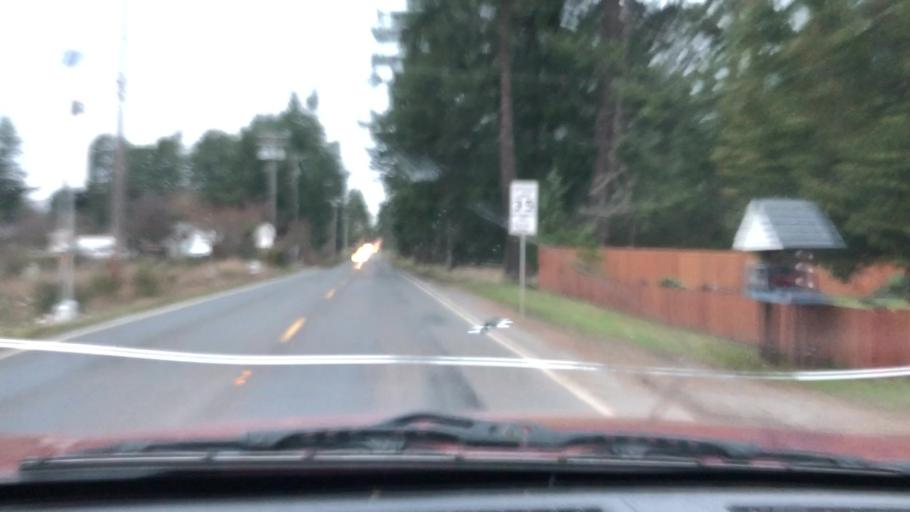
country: US
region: Washington
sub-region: Pierce County
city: Elk Plain
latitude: 47.0582
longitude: -122.4003
